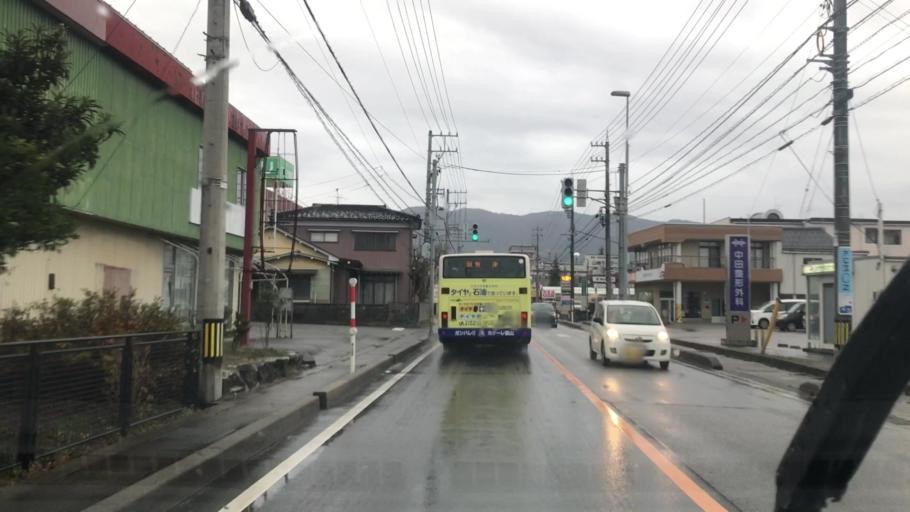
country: JP
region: Toyama
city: Yatsuomachi-higashikumisaka
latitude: 36.5813
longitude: 137.2064
